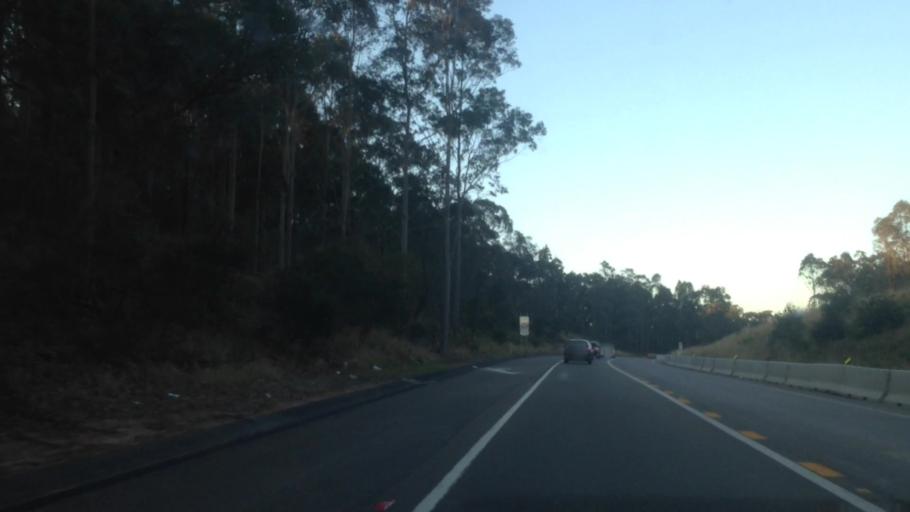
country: AU
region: New South Wales
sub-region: Wyong Shire
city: Jilliby
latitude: -33.2177
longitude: 151.4407
